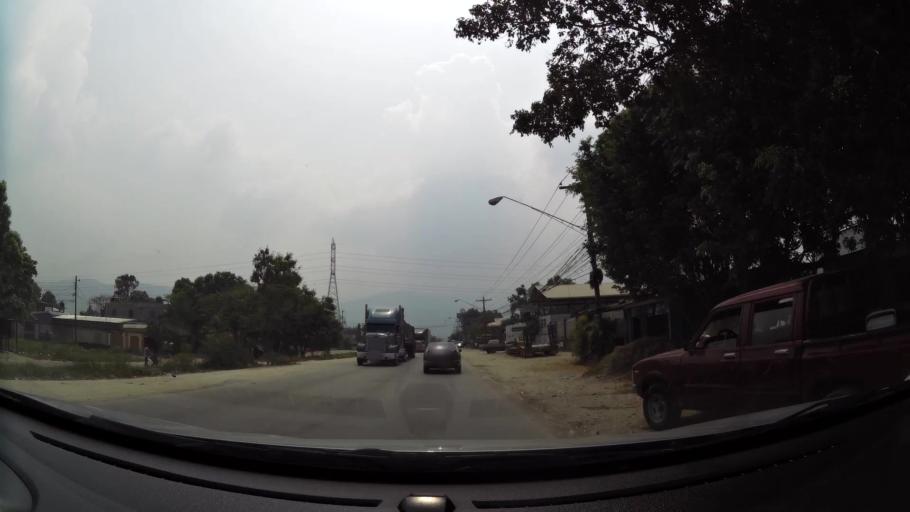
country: HN
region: Cortes
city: San Pedro Sula
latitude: 15.4716
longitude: -88.0014
